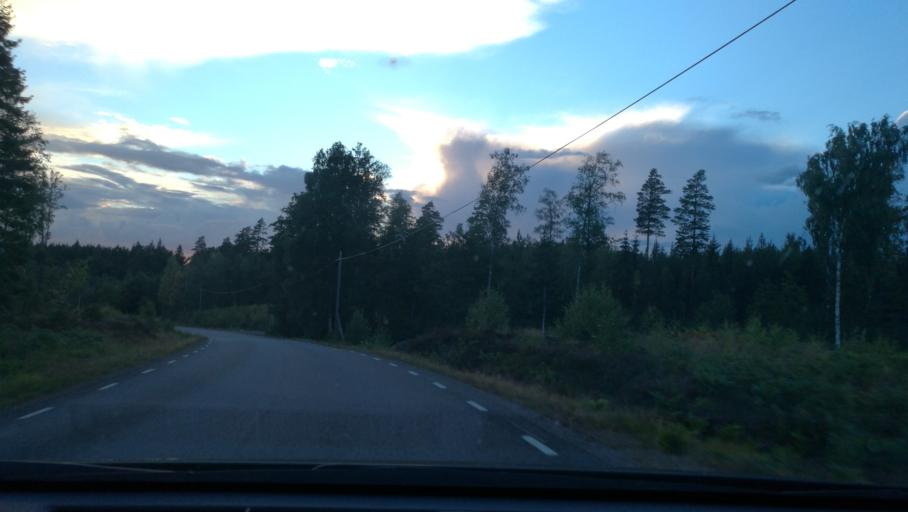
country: SE
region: OEstergoetland
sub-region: Norrkopings Kommun
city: Jursla
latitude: 58.8049
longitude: 16.1265
